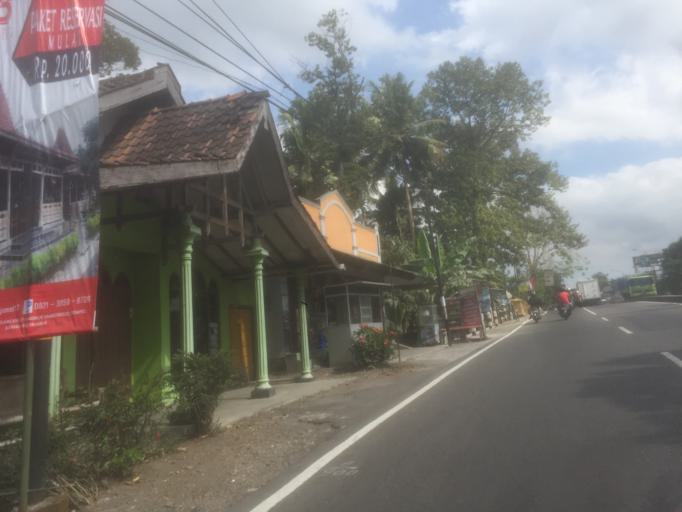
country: ID
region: Daerah Istimewa Yogyakarta
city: Sleman
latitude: -7.6710
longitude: 110.3345
